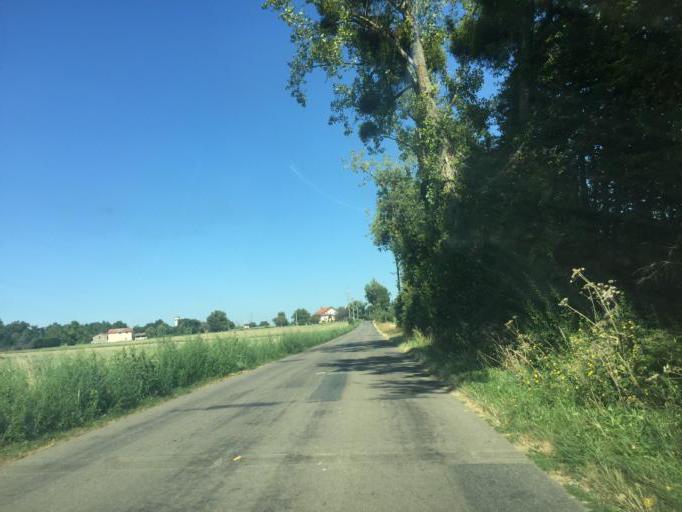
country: FR
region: Rhone-Alpes
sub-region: Departement de l'Ain
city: Saint-Andre-de-Corcy
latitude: 45.9117
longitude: 4.9570
